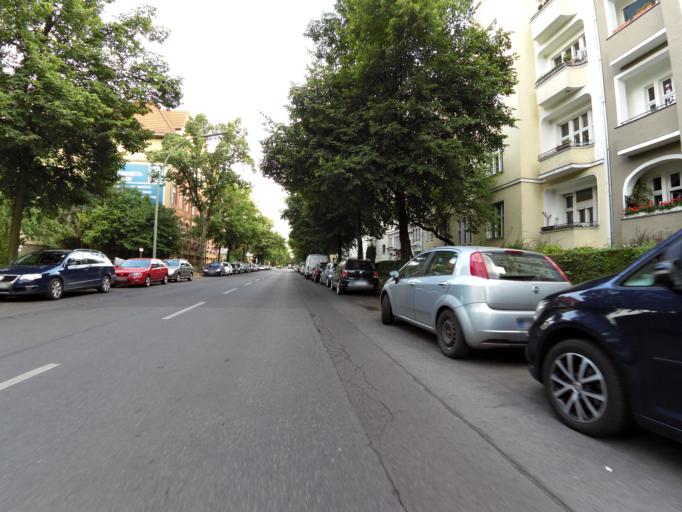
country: DE
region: Berlin
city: Schoneberg Bezirk
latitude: 52.4645
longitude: 13.3445
